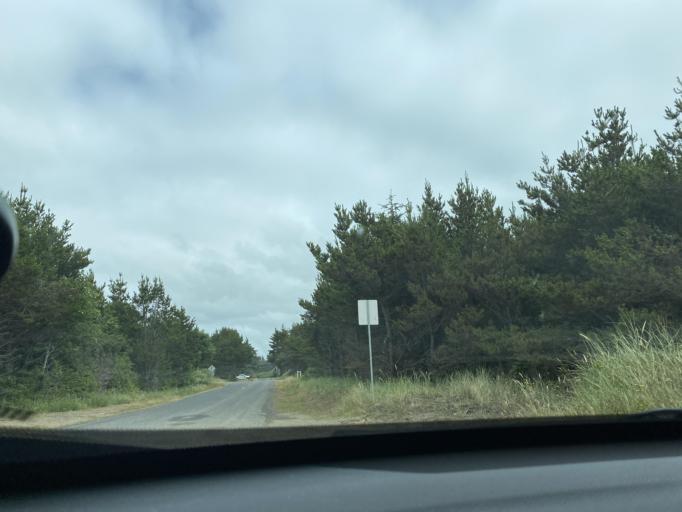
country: US
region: Washington
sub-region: Grays Harbor County
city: Ocean Shores
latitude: 47.1142
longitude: -124.1796
